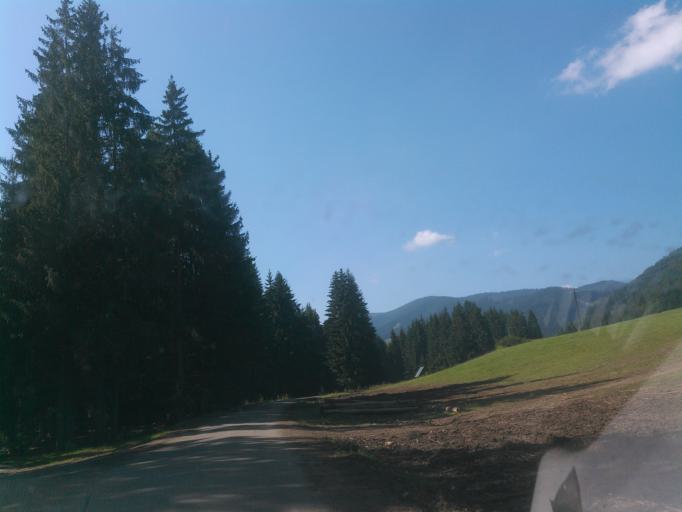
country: SK
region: Zilinsky
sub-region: Okres Liptovsky Mikulas
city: Liptovsky Mikulas
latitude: 49.0102
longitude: 19.5181
